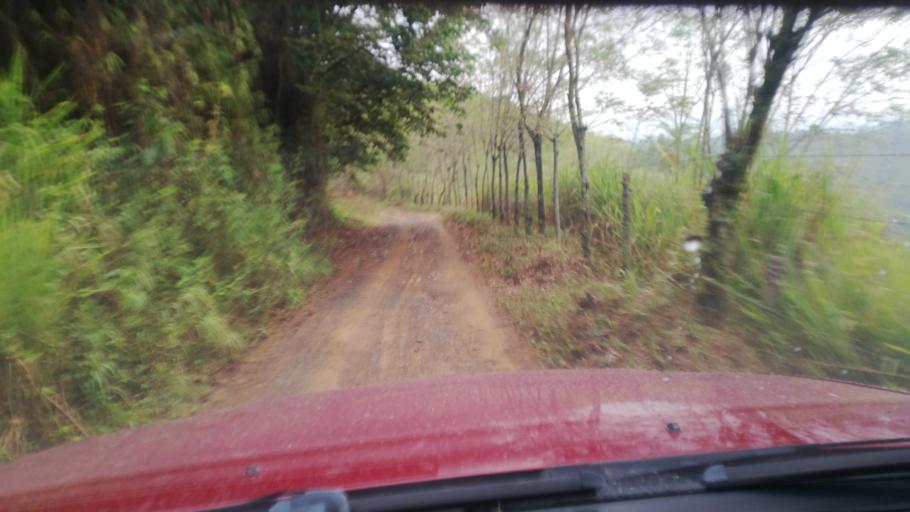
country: CO
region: Risaralda
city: Balboa
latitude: 4.8888
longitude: -75.9668
